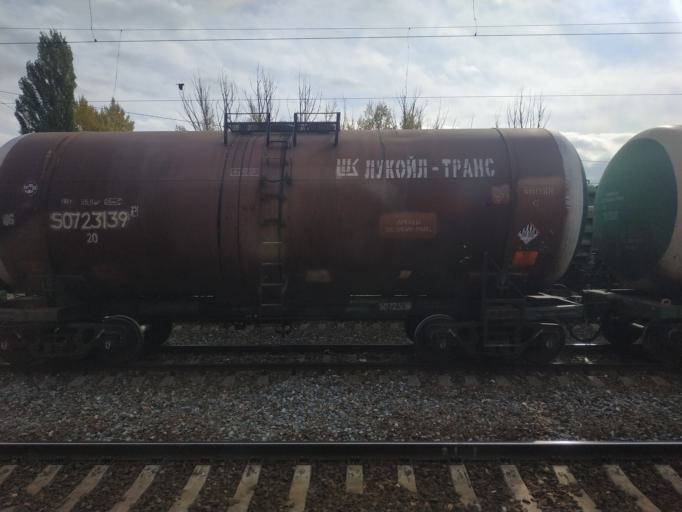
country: RU
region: Volgograd
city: Volgograd
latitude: 48.6685
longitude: 44.4603
